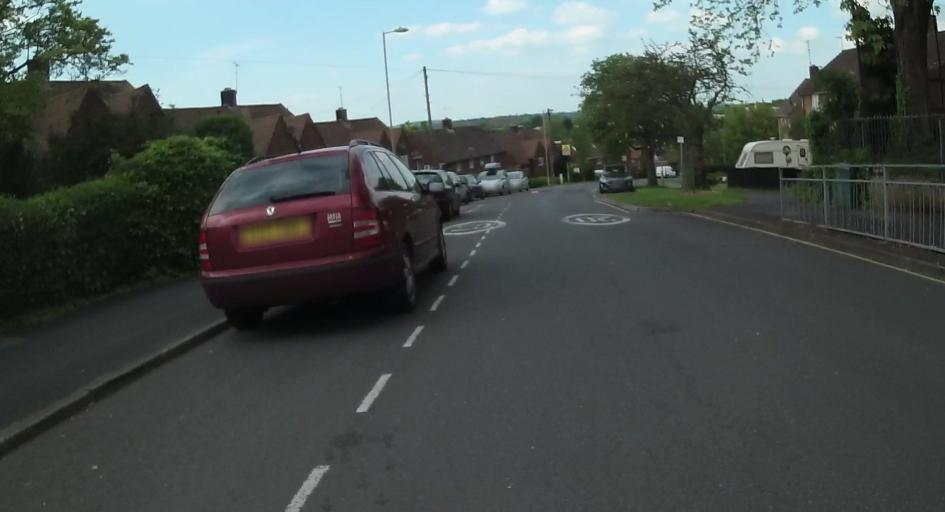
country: GB
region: England
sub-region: Hampshire
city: Winchester
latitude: 51.0635
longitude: -1.2990
